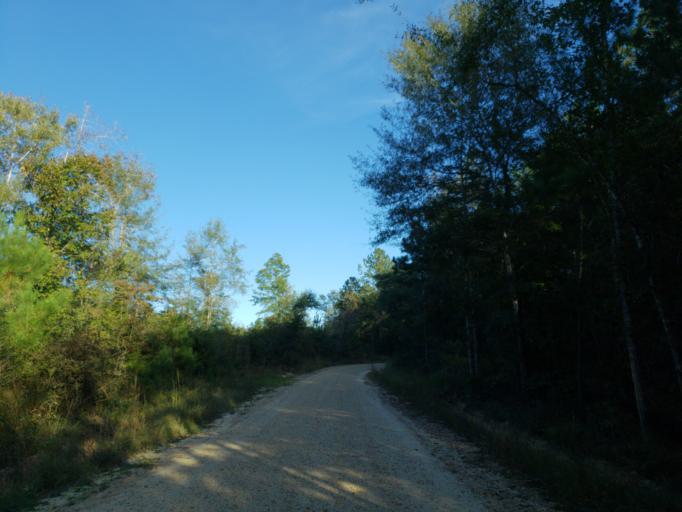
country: US
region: Mississippi
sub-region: Perry County
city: Richton
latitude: 31.3539
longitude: -88.8110
